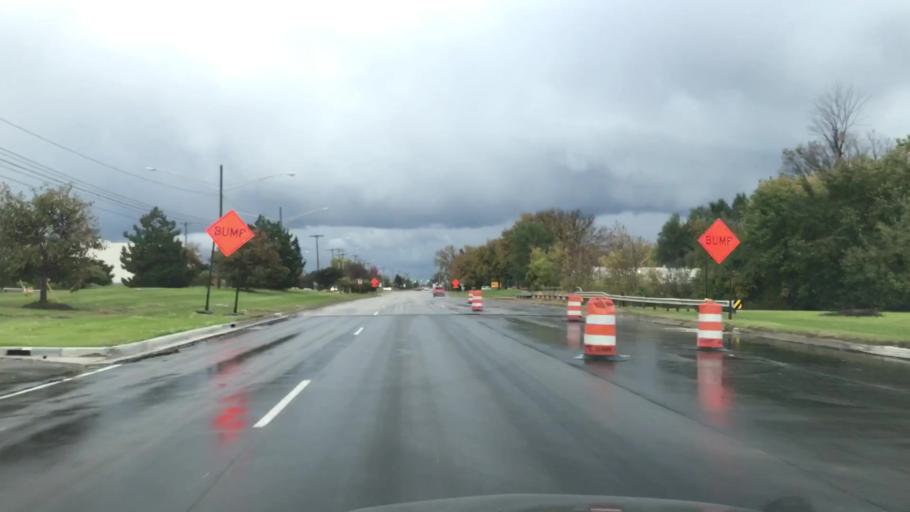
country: US
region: Michigan
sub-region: Macomb County
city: Sterling Heights
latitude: 42.5438
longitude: -83.0483
